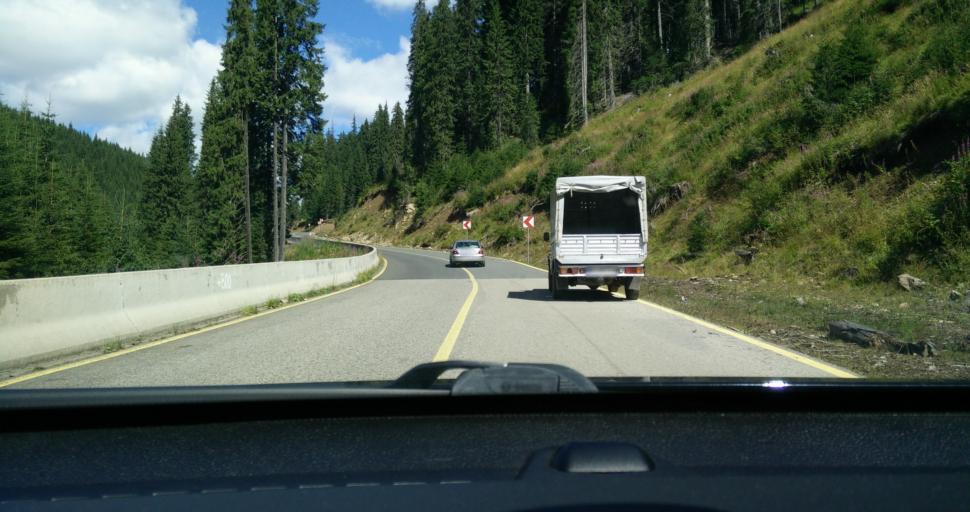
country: RO
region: Hunedoara
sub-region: Oras Petrila
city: Petrila
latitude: 45.4402
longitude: 23.6277
